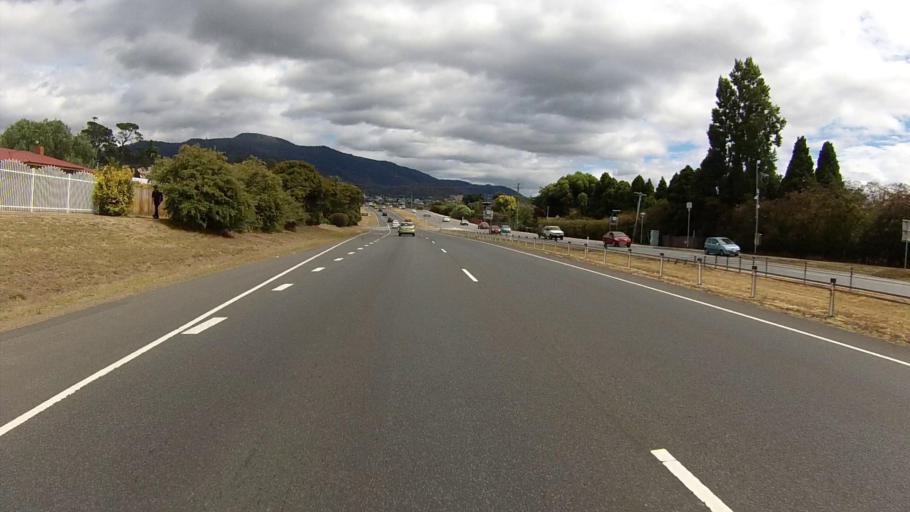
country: AU
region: Tasmania
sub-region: Glenorchy
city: Berriedale
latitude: -42.8205
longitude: 147.2646
